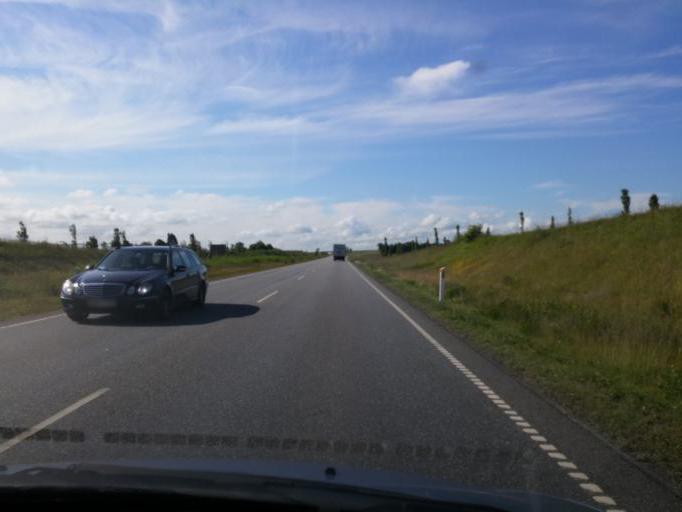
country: DK
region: South Denmark
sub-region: Odense Kommune
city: Bullerup
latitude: 55.4076
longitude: 10.4726
